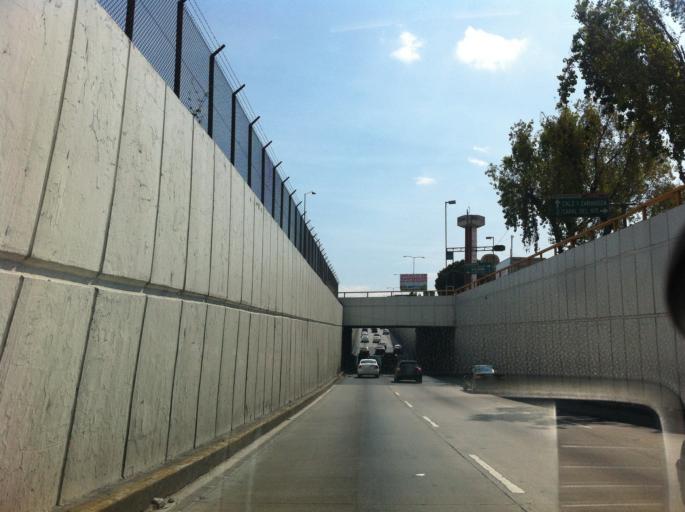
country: MX
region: Mexico City
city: Cuauhtemoc
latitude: 19.4602
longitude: -99.1236
